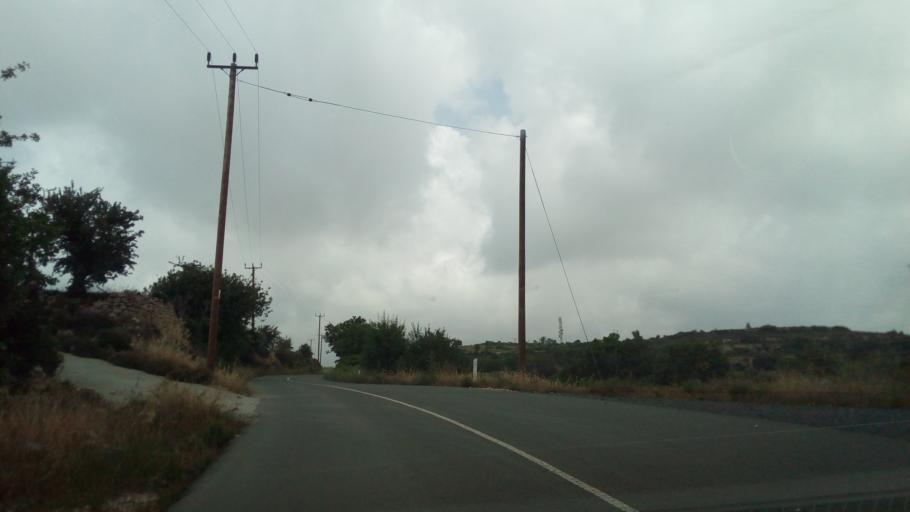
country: CY
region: Limassol
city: Pachna
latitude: 34.8213
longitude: 32.8661
